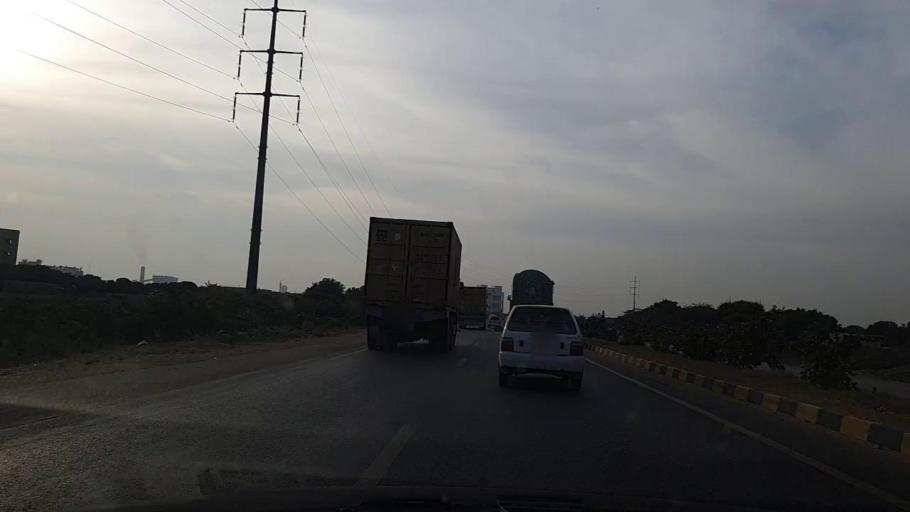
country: PK
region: Sindh
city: Gharo
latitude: 24.8388
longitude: 67.4364
